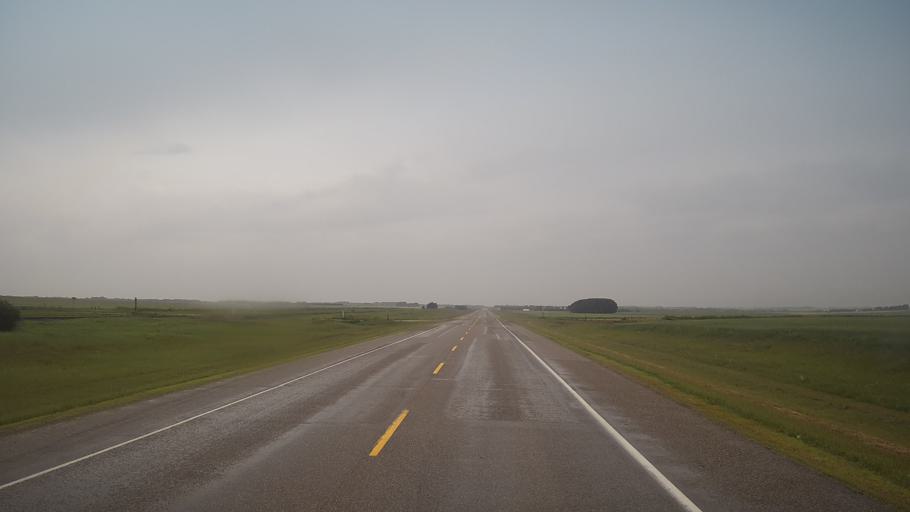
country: CA
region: Saskatchewan
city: Wilkie
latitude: 52.2244
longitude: -108.5248
